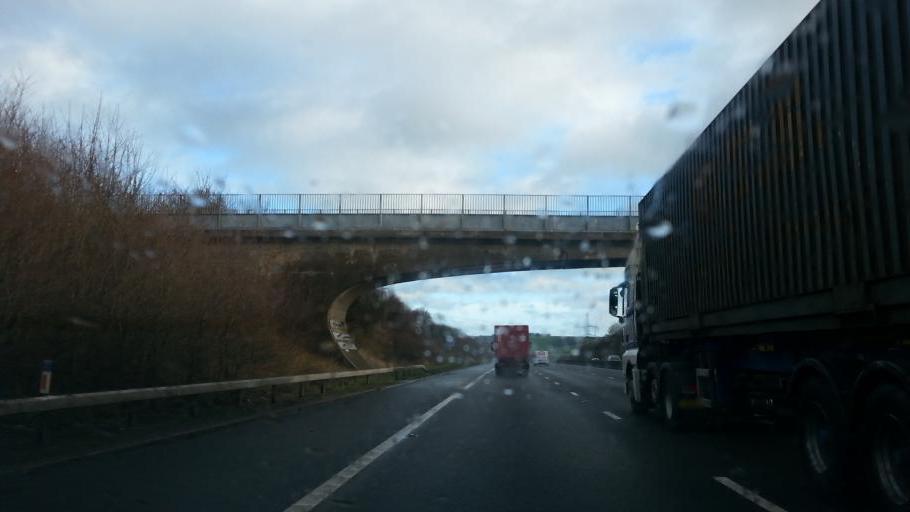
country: GB
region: England
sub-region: South Gloucestershire
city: Pucklechurch
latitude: 51.4980
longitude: -2.4108
